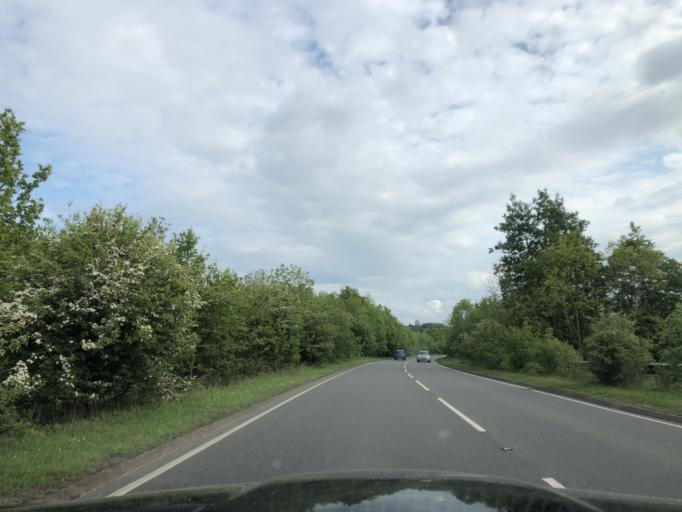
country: GB
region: England
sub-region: Warwickshire
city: Wellesbourne Mountford
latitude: 52.1356
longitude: -1.6147
